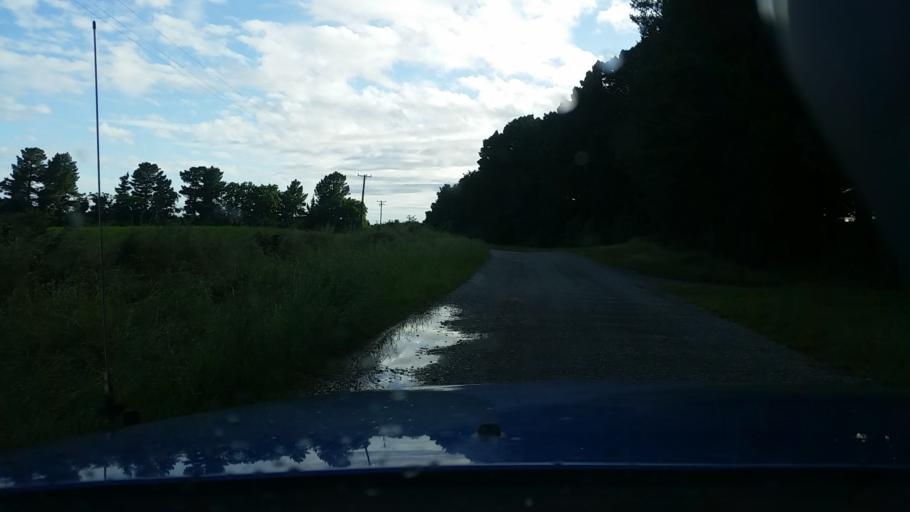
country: NZ
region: Canterbury
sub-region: Ashburton District
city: Rakaia
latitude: -43.7628
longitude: 172.0243
